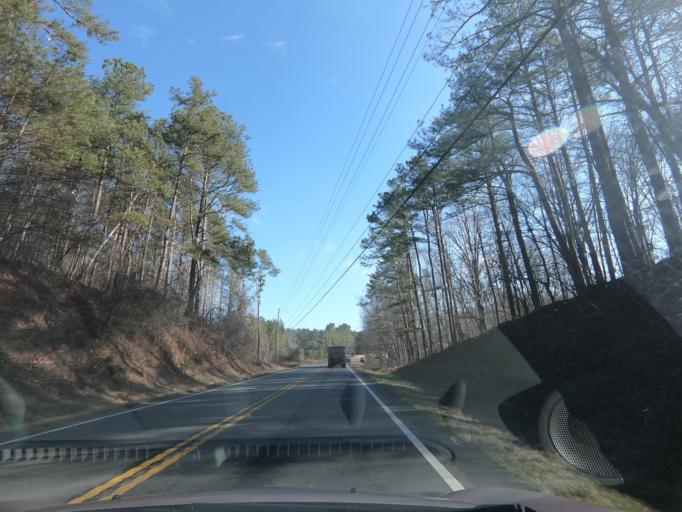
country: US
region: Georgia
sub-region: Cherokee County
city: Ball Ground
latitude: 34.2982
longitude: -84.2512
